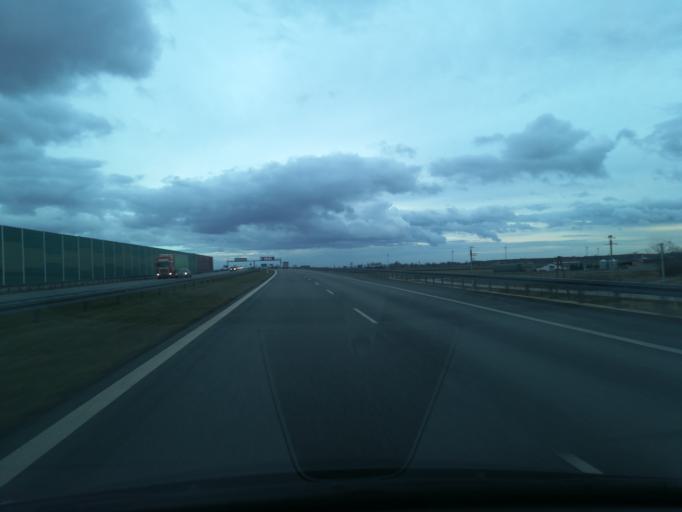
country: PL
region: Lodz Voivodeship
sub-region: Powiat kutnowski
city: Krzyzanow
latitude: 52.2358
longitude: 19.4538
